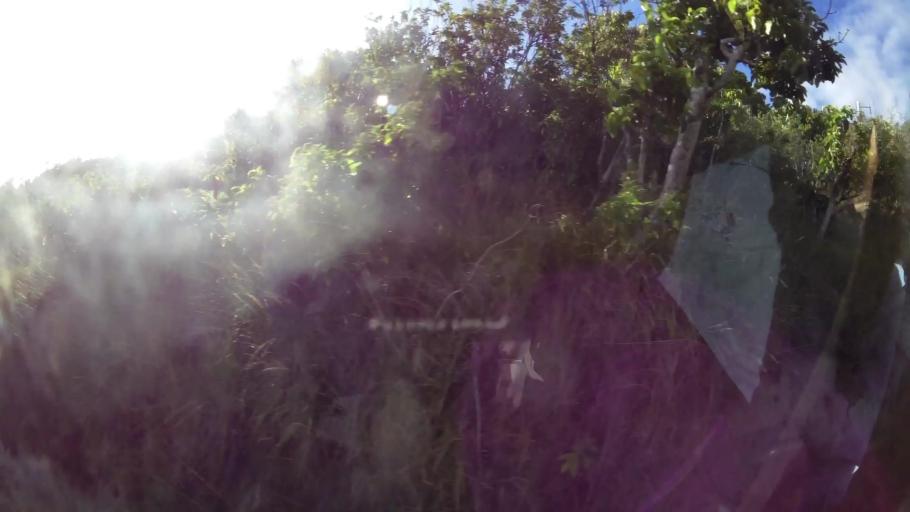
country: MS
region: Saint Peter
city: Brades
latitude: 16.8108
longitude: -62.1923
